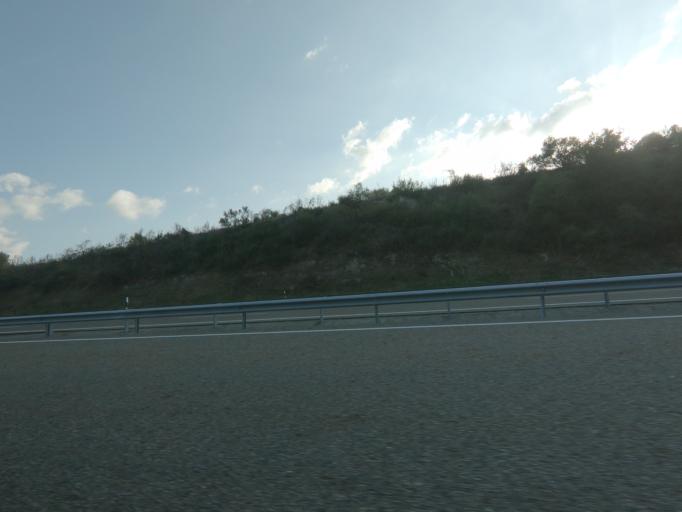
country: ES
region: Galicia
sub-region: Provincia de Ourense
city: Cualedro
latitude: 41.9966
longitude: -7.5603
